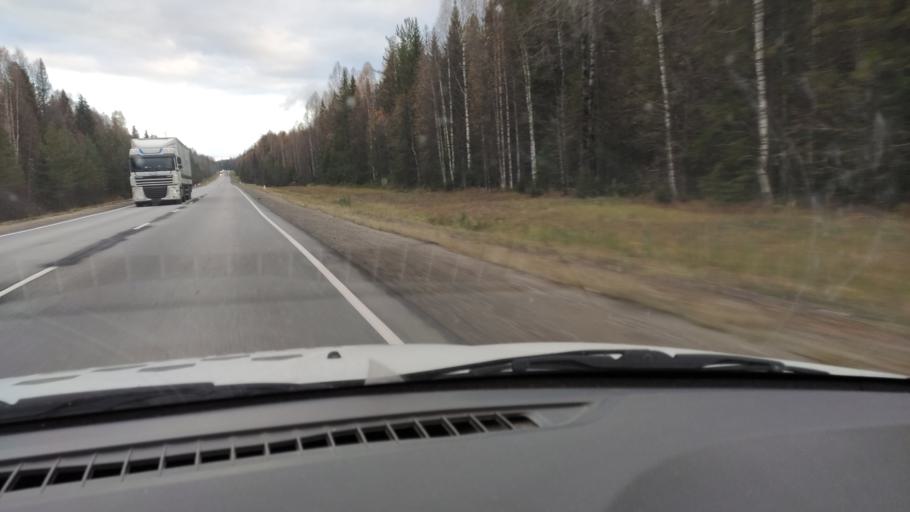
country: RU
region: Kirov
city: Chernaya Kholunitsa
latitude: 58.8417
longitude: 51.7496
